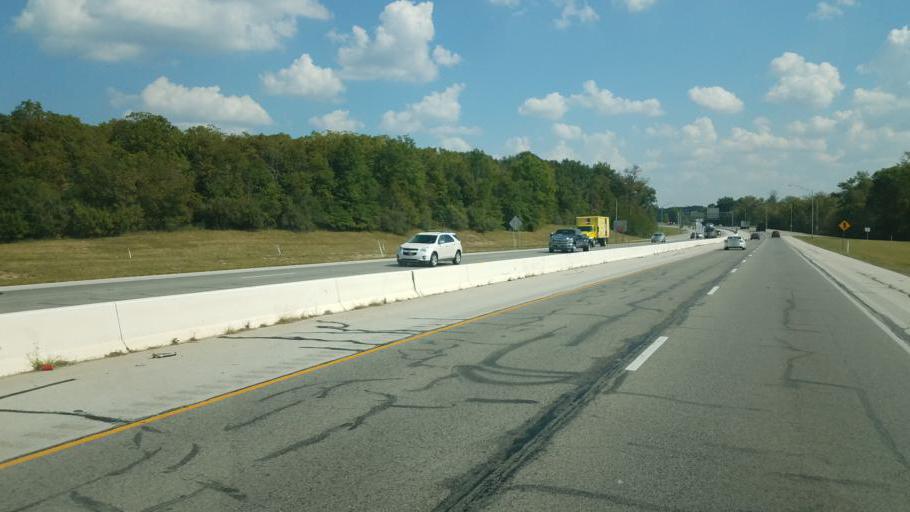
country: US
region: Indiana
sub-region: Allen County
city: Leo-Cedarville
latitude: 41.1586
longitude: -85.0597
